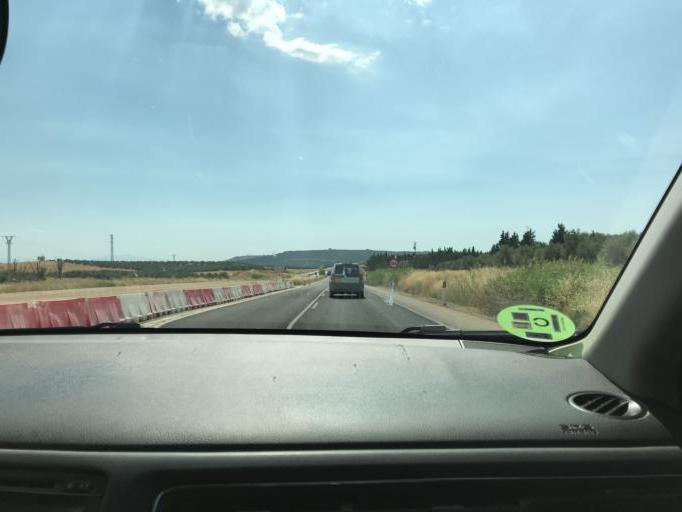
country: ES
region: Andalusia
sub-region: Provincia de Jaen
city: Ubeda
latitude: 38.0215
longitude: -3.3920
